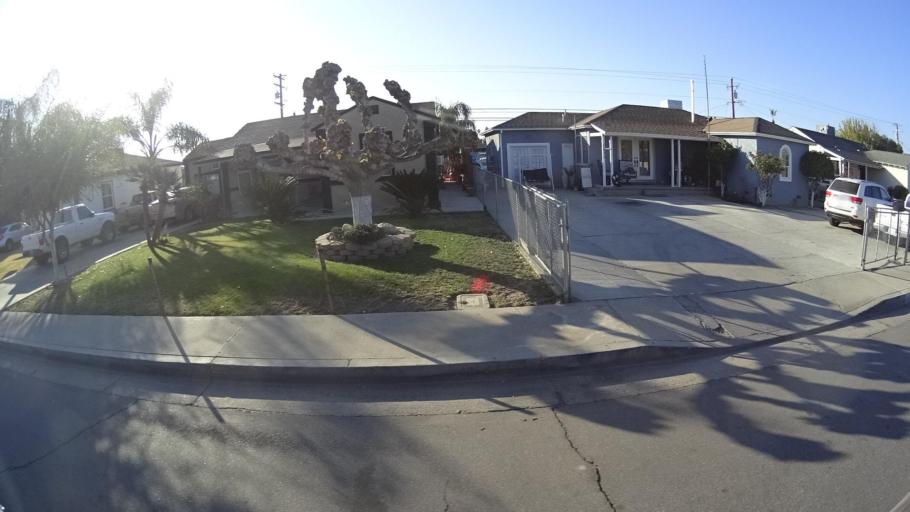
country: US
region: California
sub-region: Kern County
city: Delano
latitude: 35.7686
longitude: -119.2350
